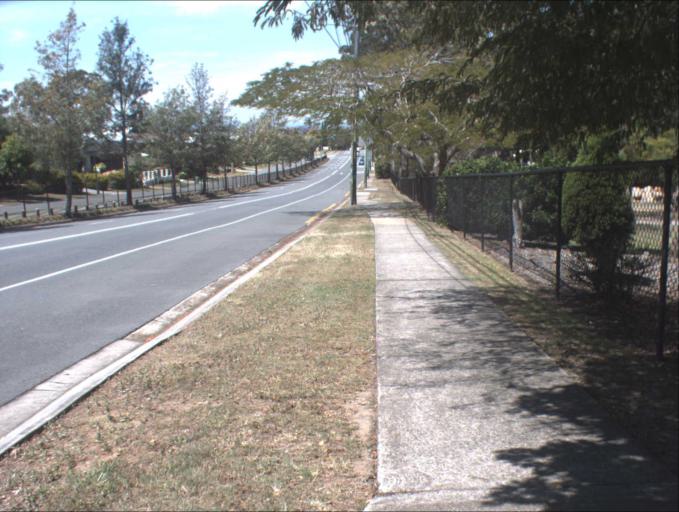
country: AU
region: Queensland
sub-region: Logan
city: Slacks Creek
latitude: -27.6337
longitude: 153.1552
